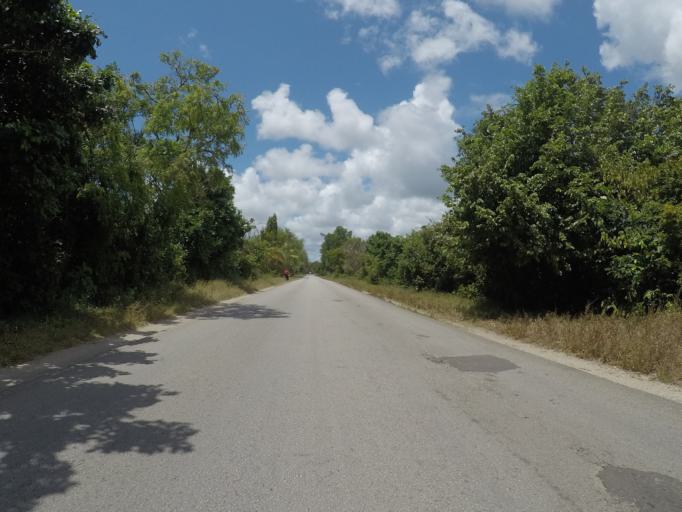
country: TZ
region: Zanzibar Central/South
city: Nganane
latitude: -6.2788
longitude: 39.4327
